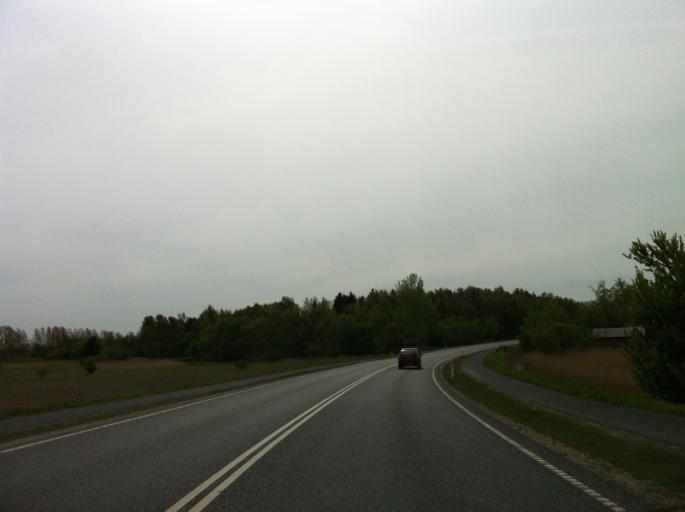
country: DK
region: Zealand
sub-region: Roskilde Kommune
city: Gundsomagle
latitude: 55.7108
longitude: 12.1158
